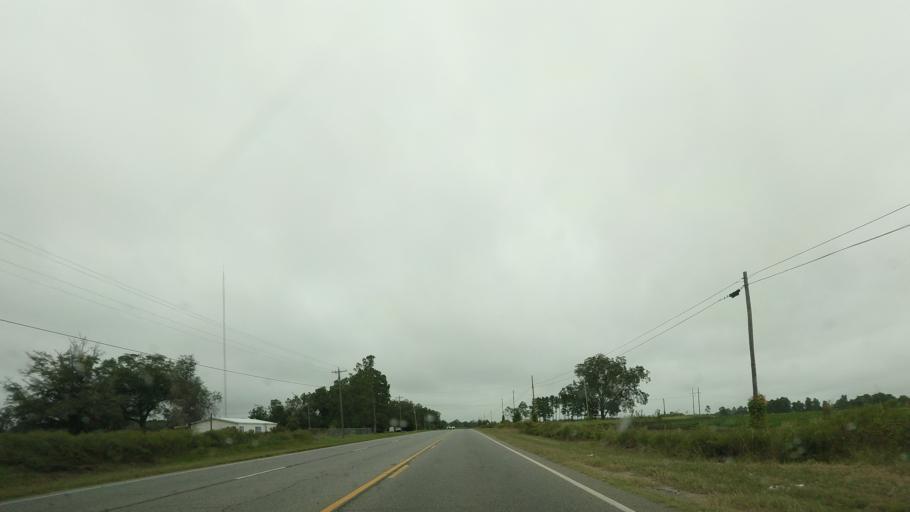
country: US
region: Georgia
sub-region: Ben Hill County
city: Fitzgerald
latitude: 31.6584
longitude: -83.2401
